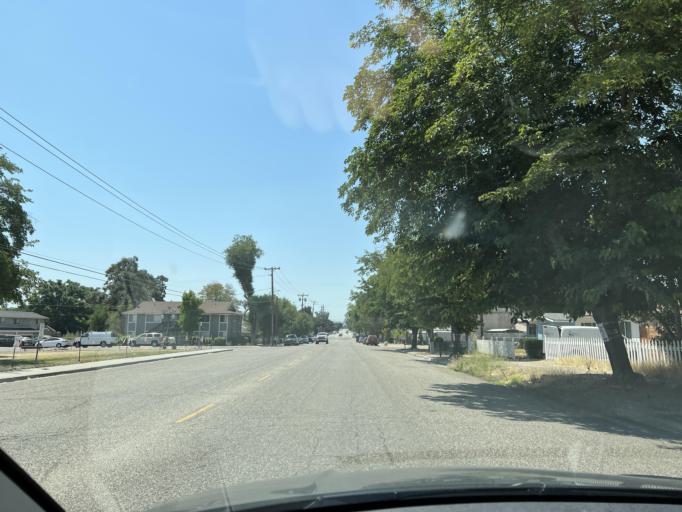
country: US
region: California
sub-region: San Luis Obispo County
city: Paso Robles
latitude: 35.6349
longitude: -120.6876
